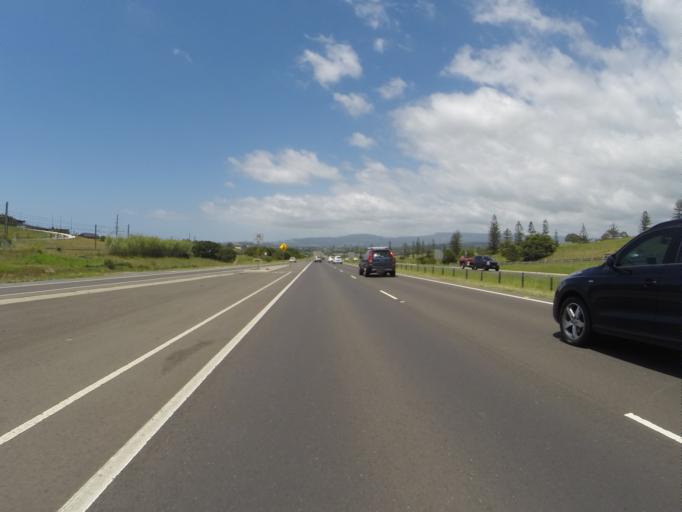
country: AU
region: New South Wales
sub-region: Shellharbour
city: Croom
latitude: -34.5916
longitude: 150.8440
